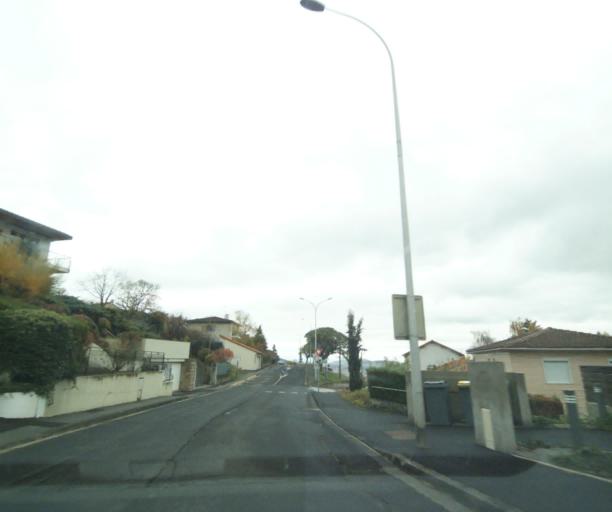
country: FR
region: Auvergne
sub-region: Departement du Puy-de-Dome
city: Beaumont
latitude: 45.7494
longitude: 3.0706
